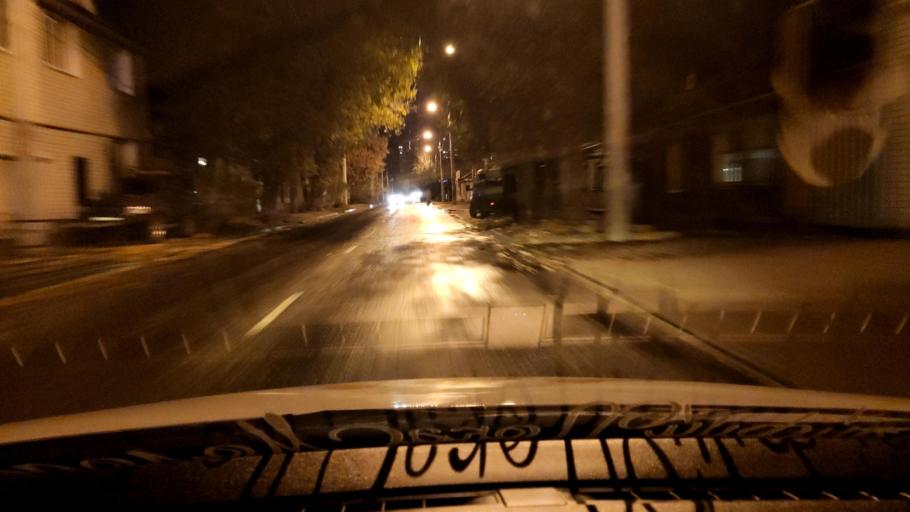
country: RU
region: Voronezj
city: Voronezh
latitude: 51.6663
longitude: 39.1679
